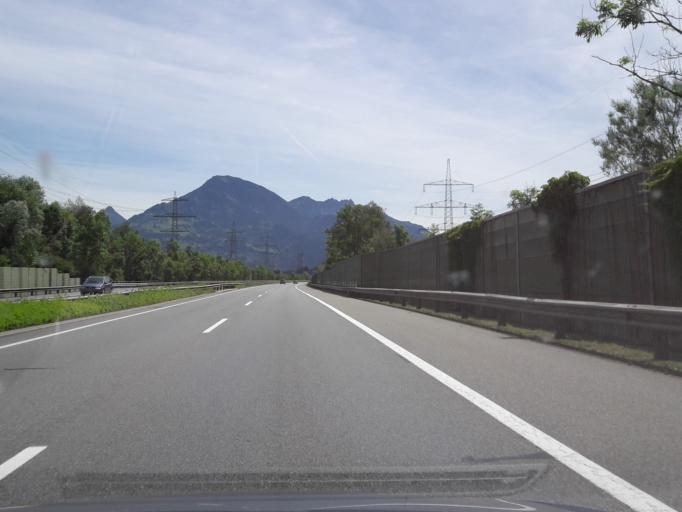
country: AT
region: Vorarlberg
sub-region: Politischer Bezirk Feldkirch
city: Schlins
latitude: 47.1961
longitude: 9.7008
